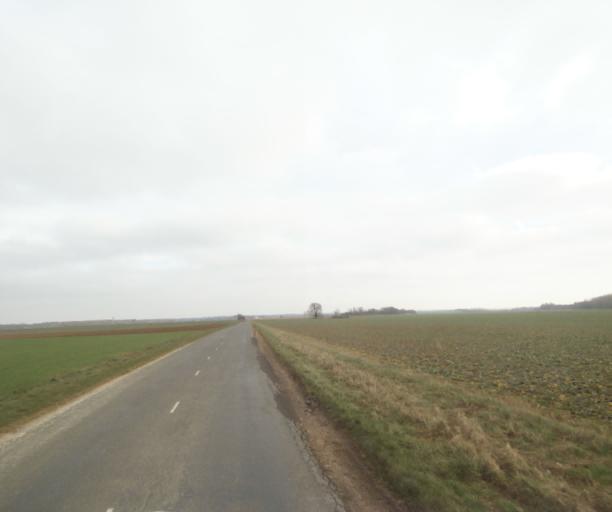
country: FR
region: Champagne-Ardenne
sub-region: Departement de la Haute-Marne
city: Villiers-en-Lieu
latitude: 48.6723
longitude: 4.8470
